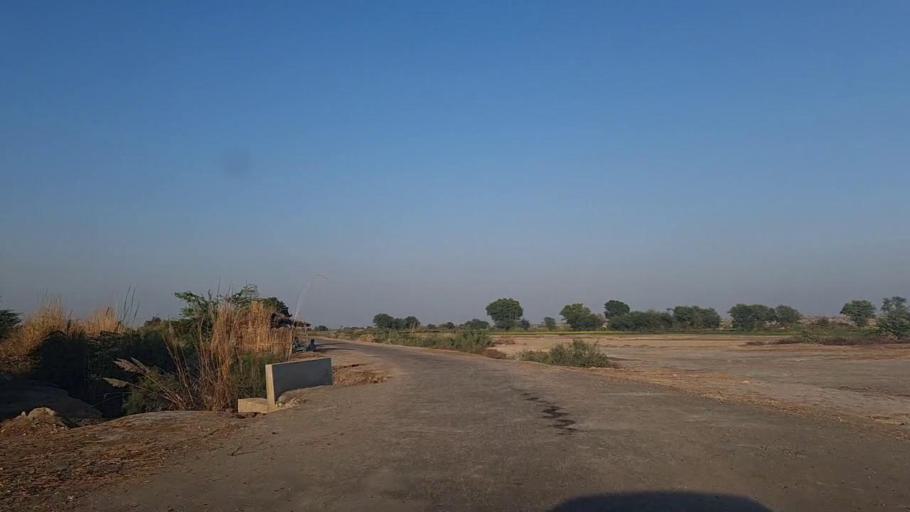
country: PK
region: Sindh
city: Jam Sahib
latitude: 26.3405
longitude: 68.6702
